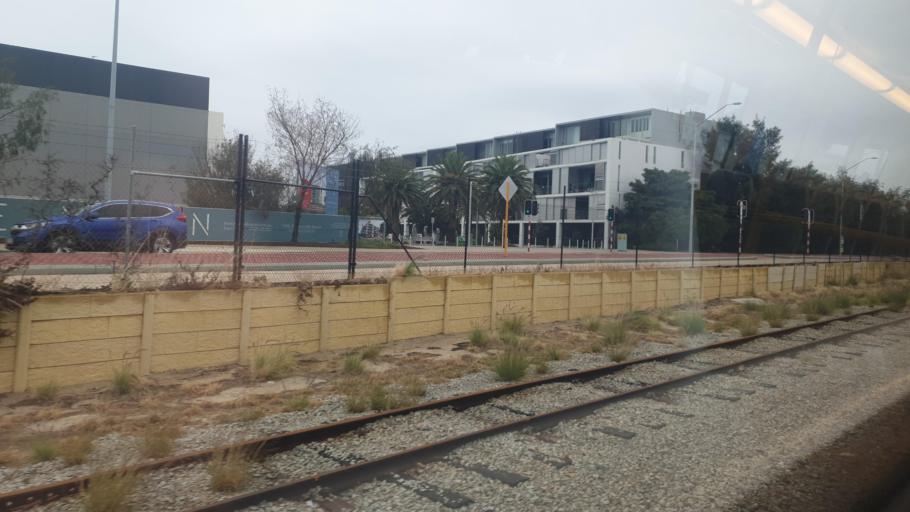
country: AU
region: Western Australia
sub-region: Fremantle
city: North Fremantle
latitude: -32.0299
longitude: 115.7518
